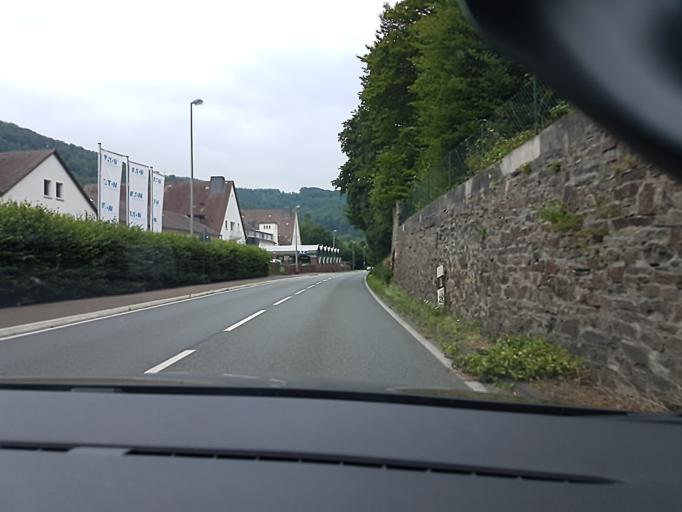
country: DE
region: Rheinland-Pfalz
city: Sulzbach
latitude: 50.3207
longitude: 7.7406
